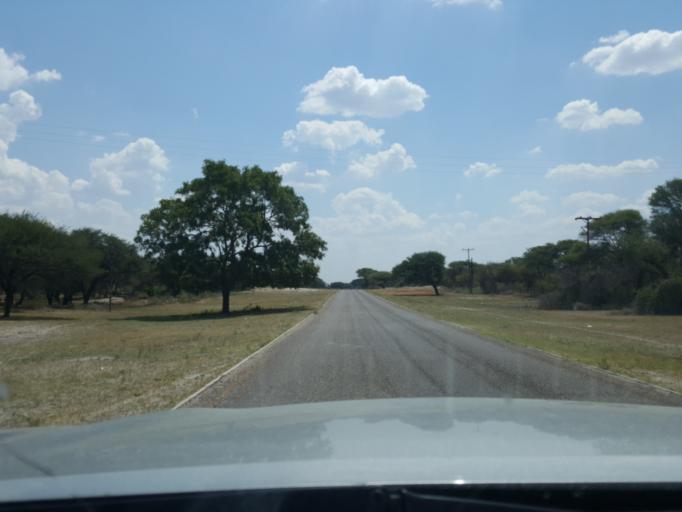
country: BW
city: Tsau
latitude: -20.1819
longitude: 22.4665
